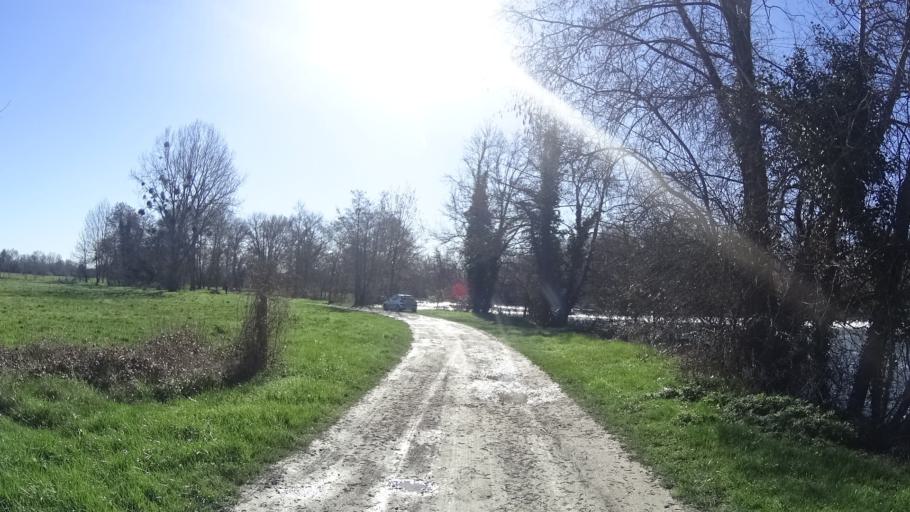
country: FR
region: Aquitaine
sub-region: Departement de la Dordogne
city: Saint-Aulaye
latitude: 45.2218
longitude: 0.1041
